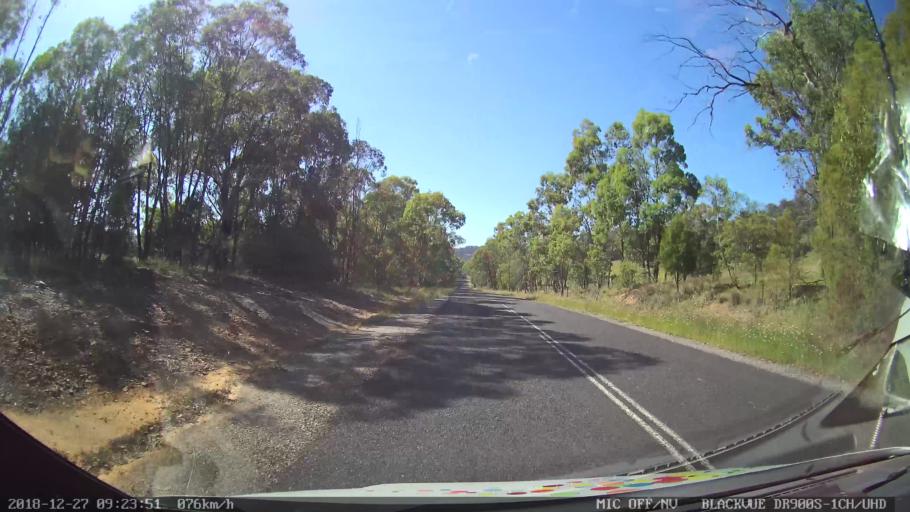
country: AU
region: New South Wales
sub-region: Lithgow
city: Portland
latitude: -33.1304
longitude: 149.9959
